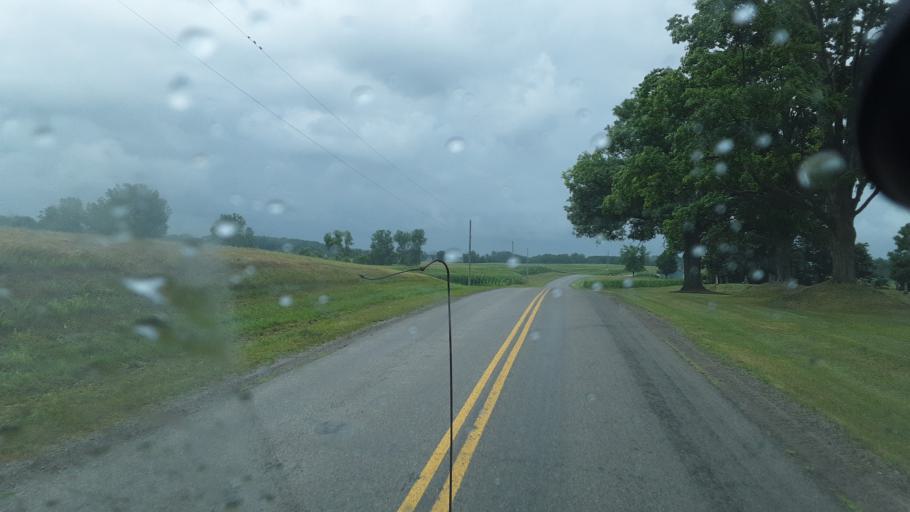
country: US
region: Indiana
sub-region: Steuben County
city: Fremont
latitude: 41.6507
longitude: -84.7922
